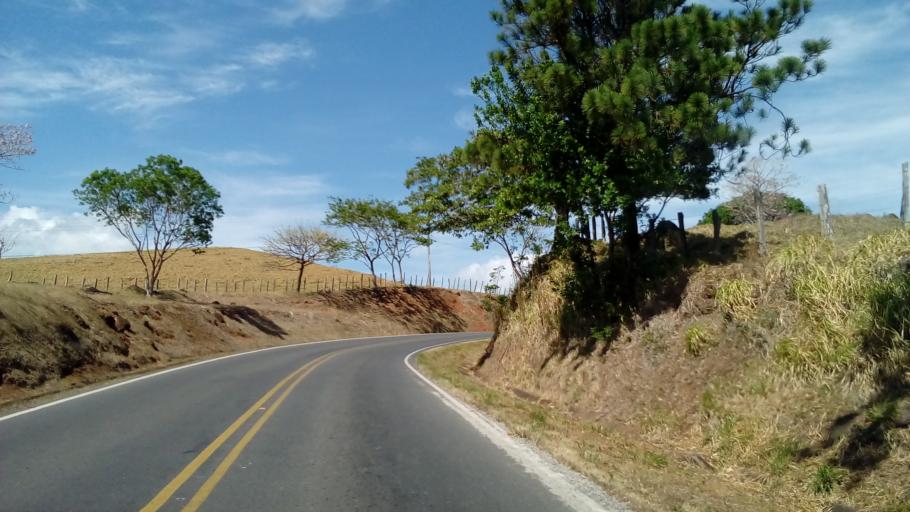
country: CR
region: Guanacaste
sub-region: Canton de Tilaran
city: Tilaran
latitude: 10.4889
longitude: -85.0077
